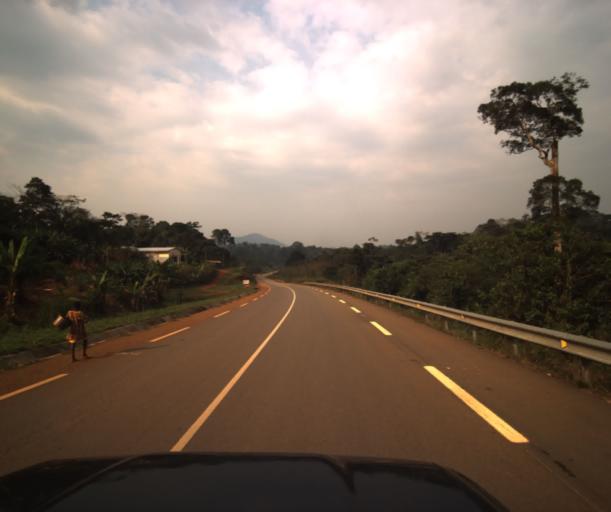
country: CM
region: Centre
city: Mbankomo
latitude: 3.7705
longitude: 11.4142
